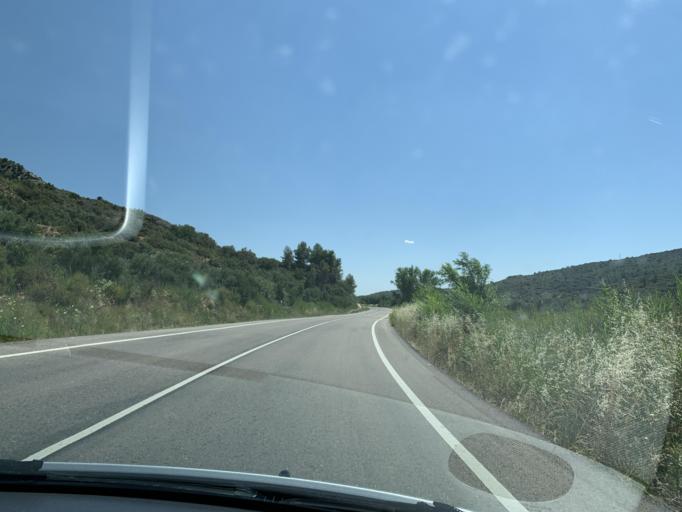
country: ES
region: Castille-La Mancha
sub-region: Provincia de Guadalajara
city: Pastrana
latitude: 40.3779
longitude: -2.9105
